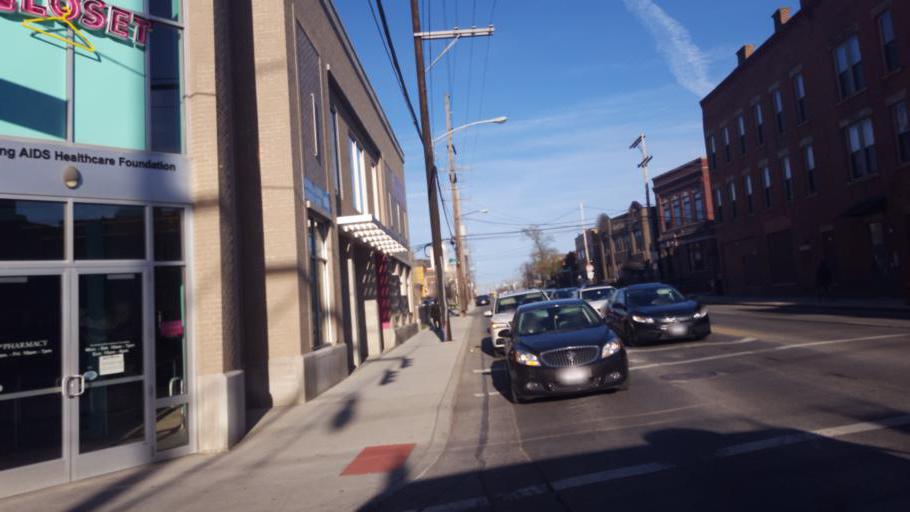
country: US
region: Ohio
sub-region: Franklin County
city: Columbus
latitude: 39.9872
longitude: -83.0055
